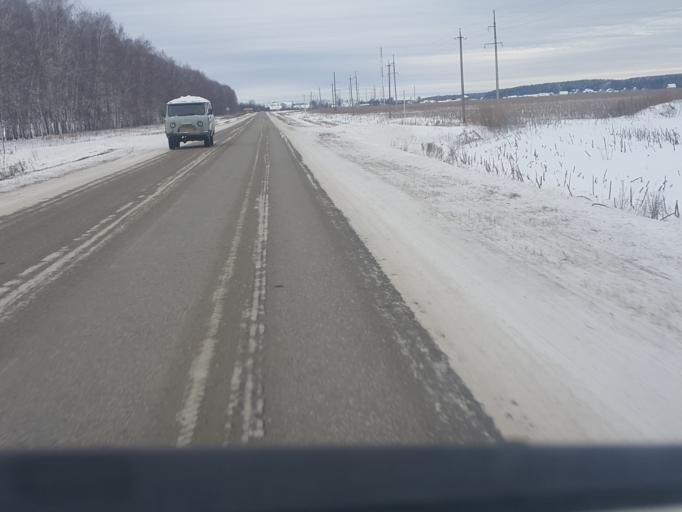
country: RU
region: Tambov
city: Rasskazovo
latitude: 52.8118
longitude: 41.7913
